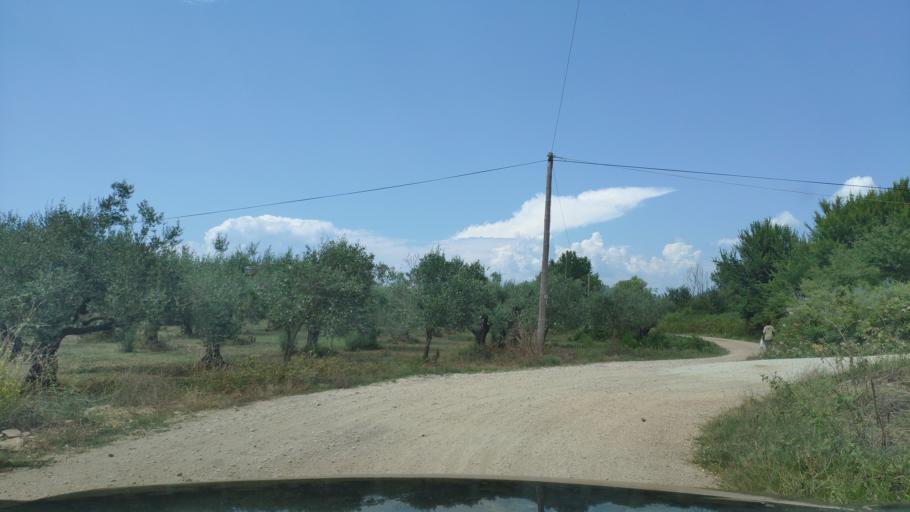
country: GR
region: West Greece
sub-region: Nomos Aitolias kai Akarnanias
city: Menidi
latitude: 39.0614
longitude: 21.0942
